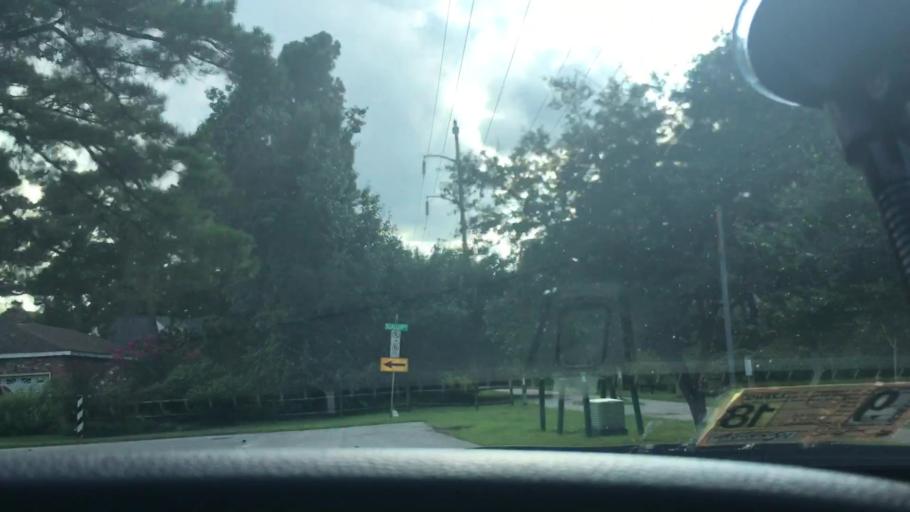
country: US
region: Virginia
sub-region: City of Virginia Beach
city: Virginia Beach
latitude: 36.9087
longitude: -76.0784
